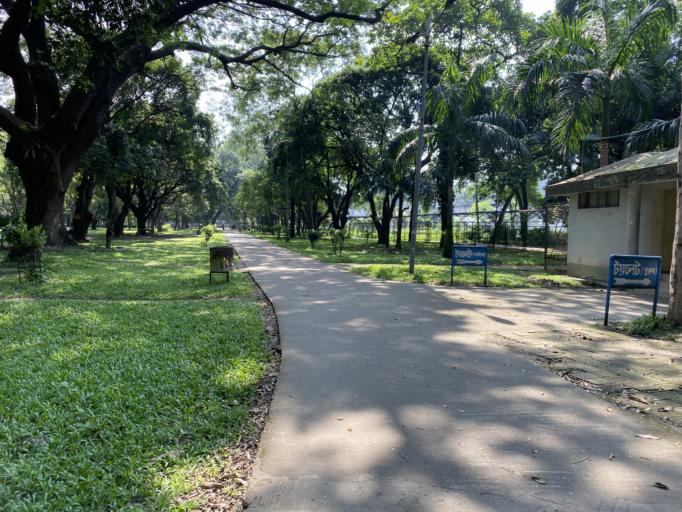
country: BD
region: Dhaka
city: Paltan
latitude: 23.7411
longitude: 90.3982
